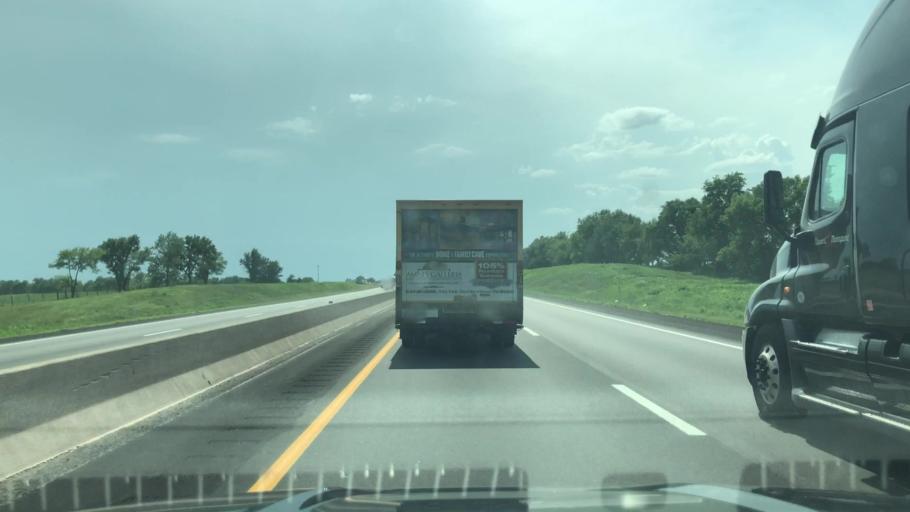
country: US
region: Oklahoma
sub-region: Craig County
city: Vinita
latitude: 36.6592
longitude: -95.0950
